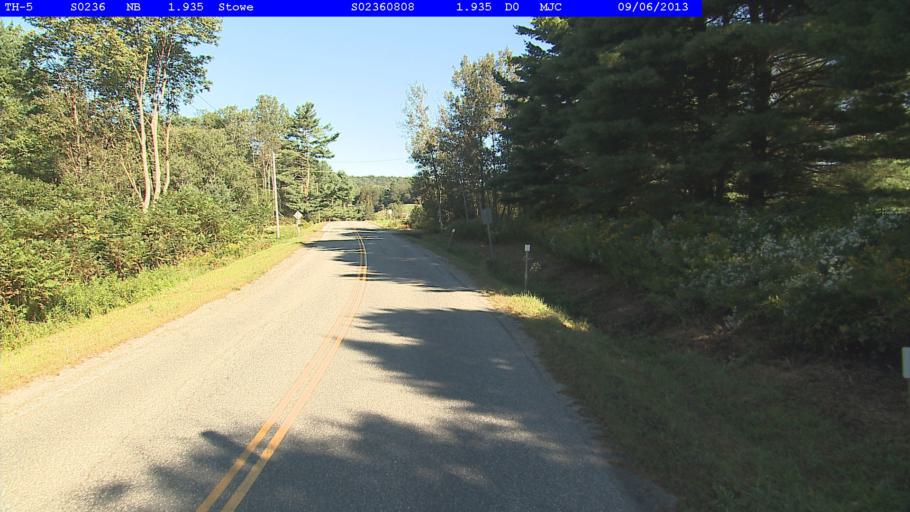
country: US
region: Vermont
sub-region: Washington County
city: Waterbury
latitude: 44.4529
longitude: -72.7288
